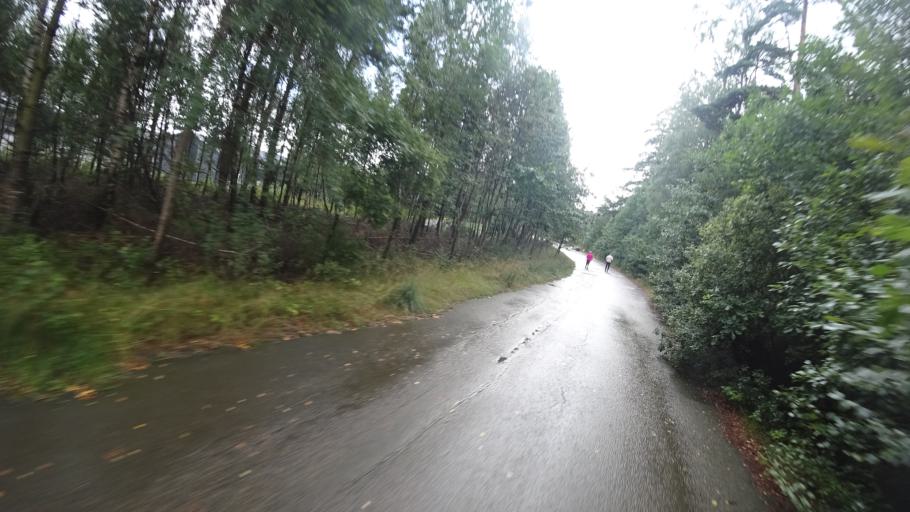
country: SE
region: Vaestra Goetaland
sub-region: Partille Kommun
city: Ojersjo
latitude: 57.6812
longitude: 12.0889
